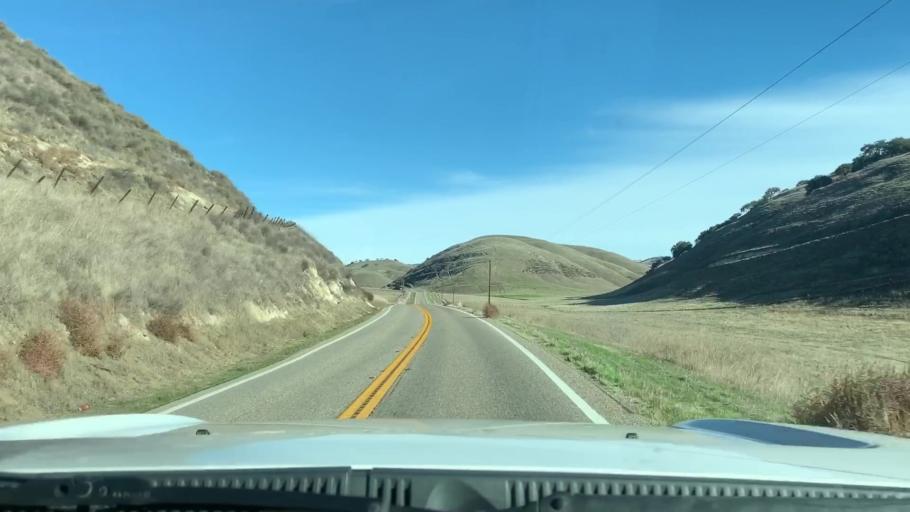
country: US
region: California
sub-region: Monterey County
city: King City
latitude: 36.1705
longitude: -120.8511
